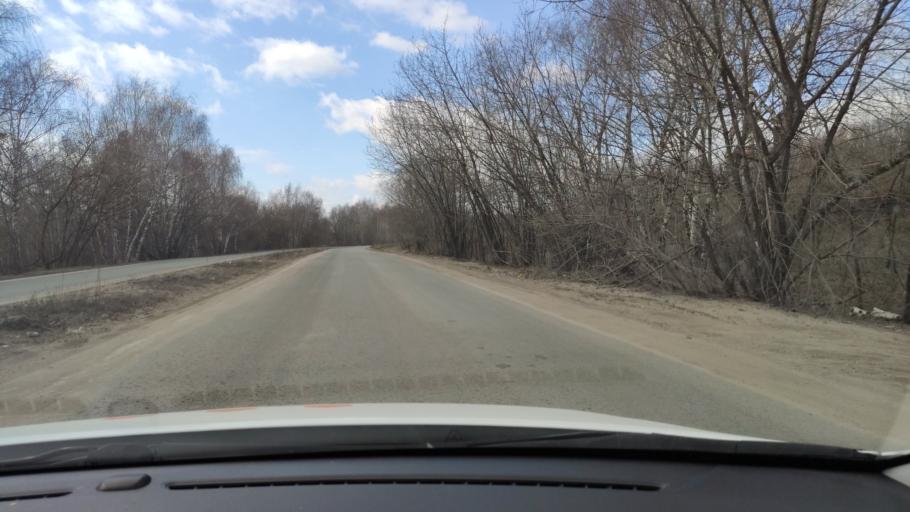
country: RU
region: Tatarstan
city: Staroye Arakchino
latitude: 55.8620
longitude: 48.9673
